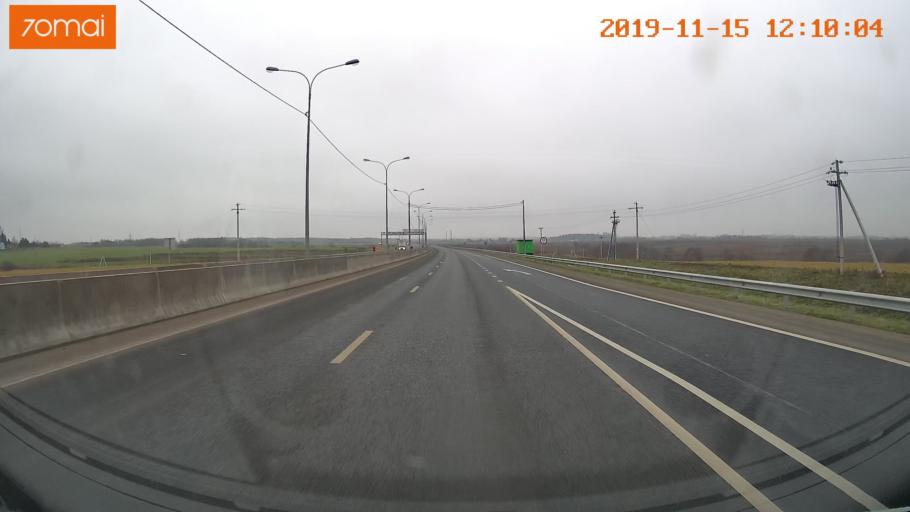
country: RU
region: Vologda
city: Molochnoye
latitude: 59.2100
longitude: 39.7647
